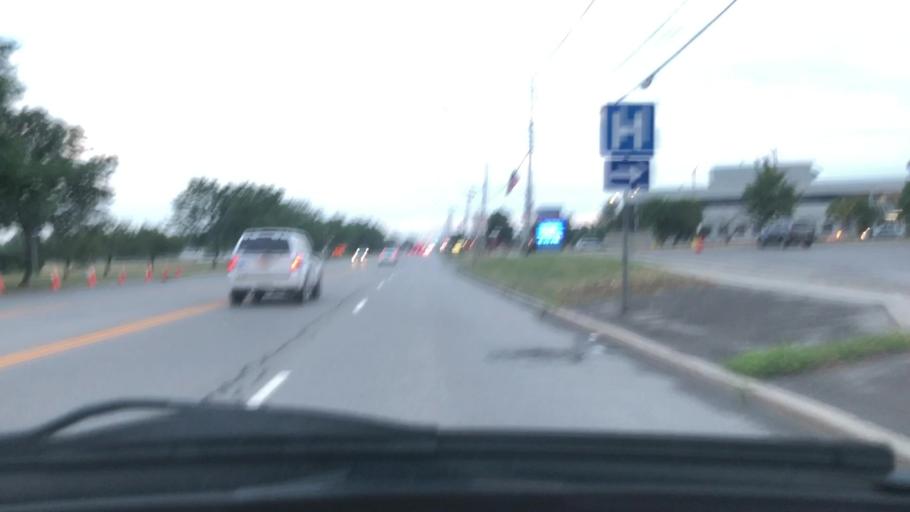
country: US
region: New York
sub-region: Erie County
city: Sloan
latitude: 42.9137
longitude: -78.7842
